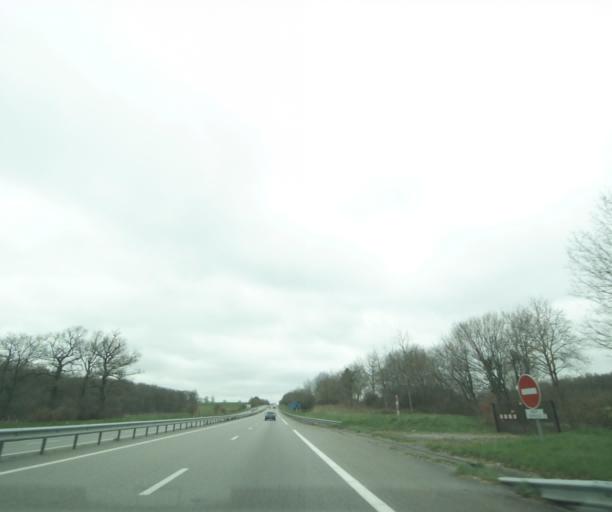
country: FR
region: Limousin
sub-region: Departement de la Haute-Vienne
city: Arnac-la-Poste
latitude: 46.2671
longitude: 1.3974
